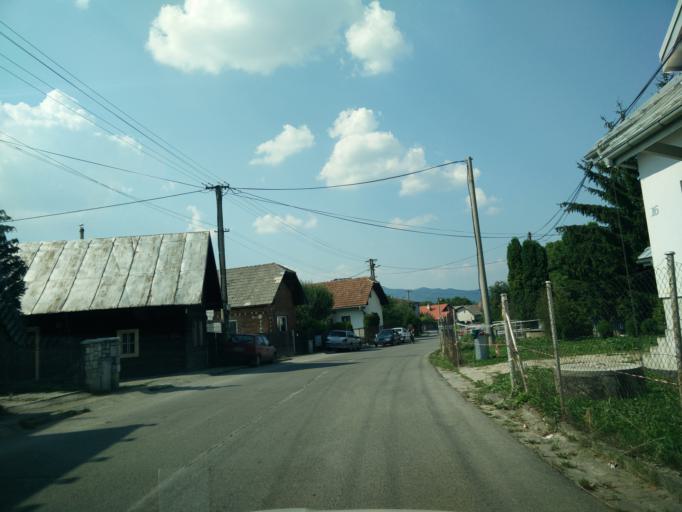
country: SK
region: Zilinsky
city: Rajec
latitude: 49.0664
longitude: 18.6491
